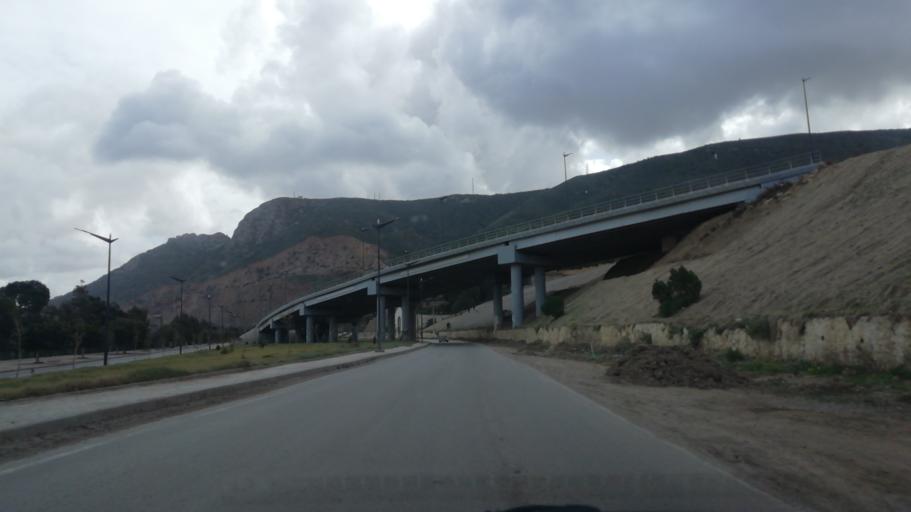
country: DZ
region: Oran
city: Mers el Kebir
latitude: 35.7155
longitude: -0.6927
